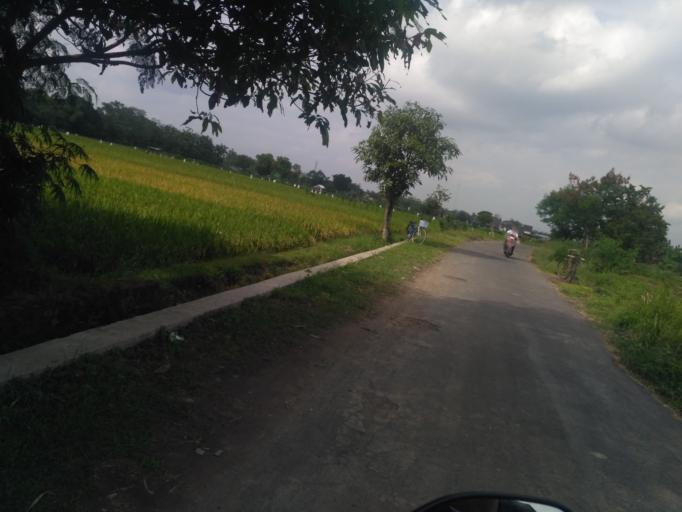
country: ID
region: Daerah Istimewa Yogyakarta
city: Yogyakarta
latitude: -7.7591
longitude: 110.3548
